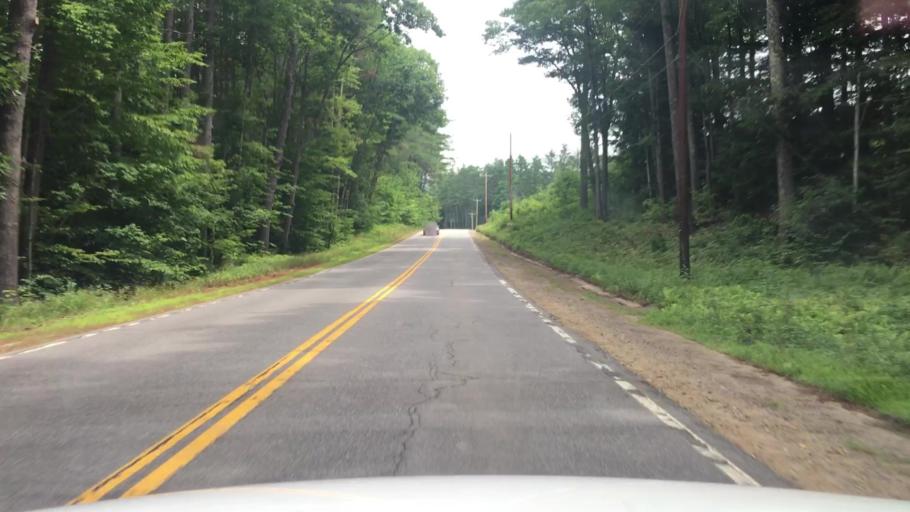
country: US
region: New Hampshire
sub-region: Grafton County
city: Plymouth
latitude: 43.7767
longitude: -71.6723
